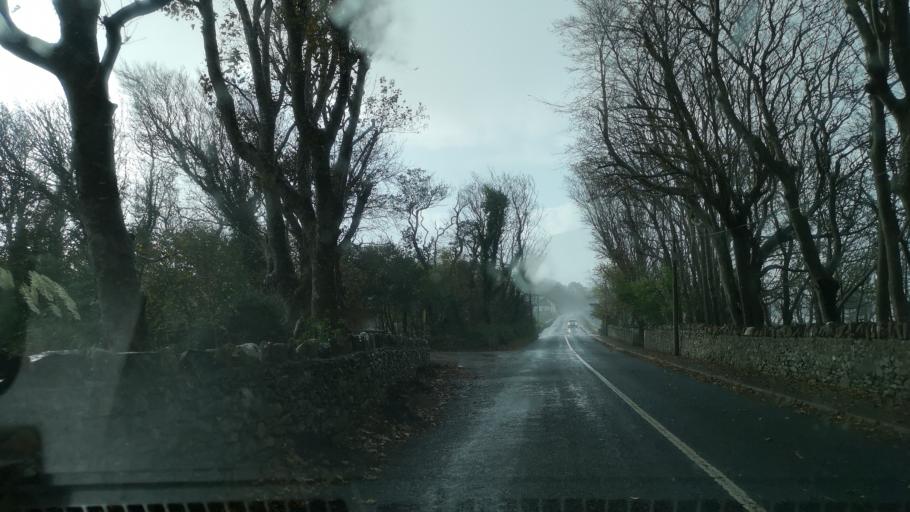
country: IE
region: Connaught
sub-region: Maigh Eo
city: Westport
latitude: 53.7894
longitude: -9.5683
